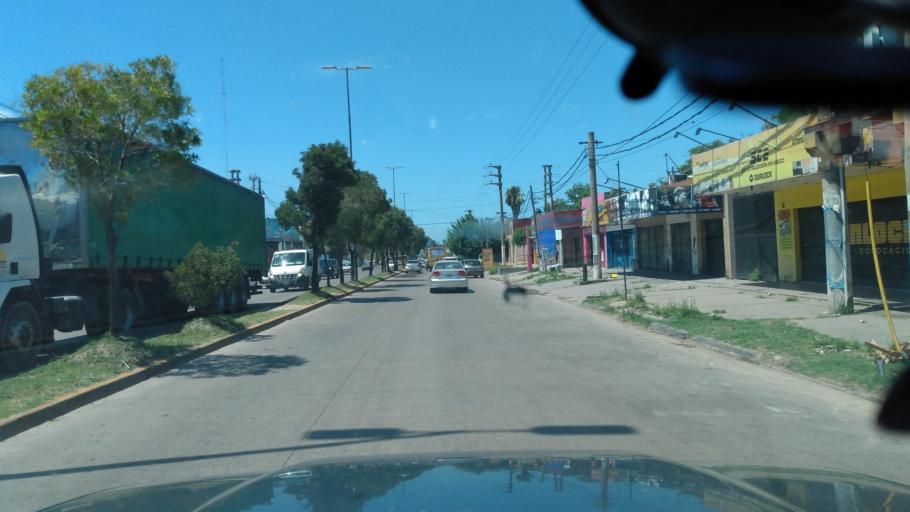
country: AR
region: Buenos Aires
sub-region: Partido de Merlo
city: Merlo
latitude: -34.5676
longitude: -58.7414
